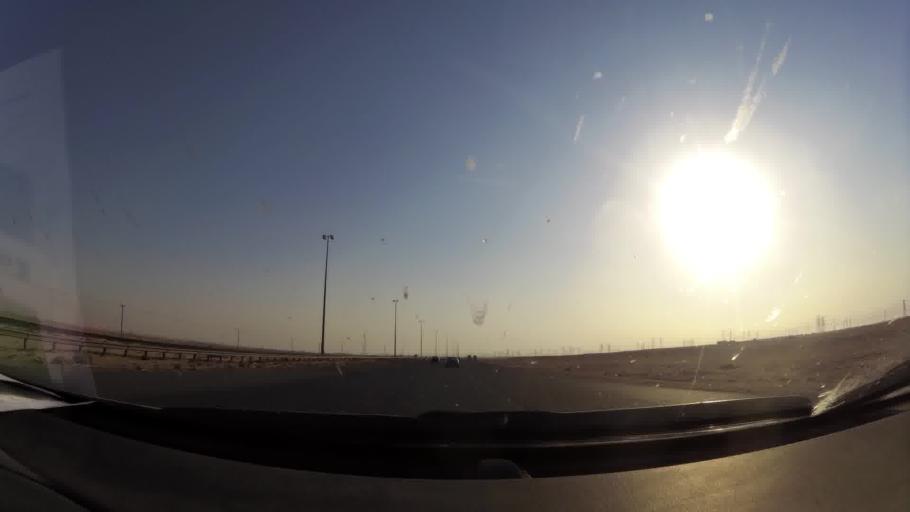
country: KW
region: Muhafazat al Jahra'
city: Al Jahra'
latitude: 29.7066
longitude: 47.6704
